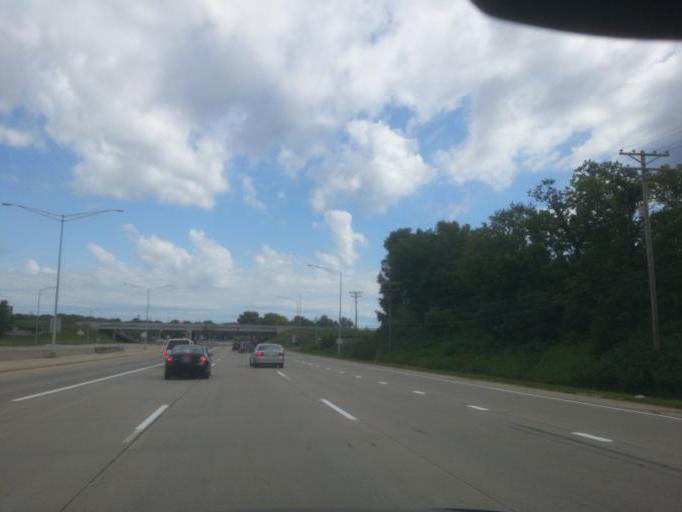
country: US
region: Wisconsin
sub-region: Dane County
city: Monona
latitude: 43.1043
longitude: -89.3164
